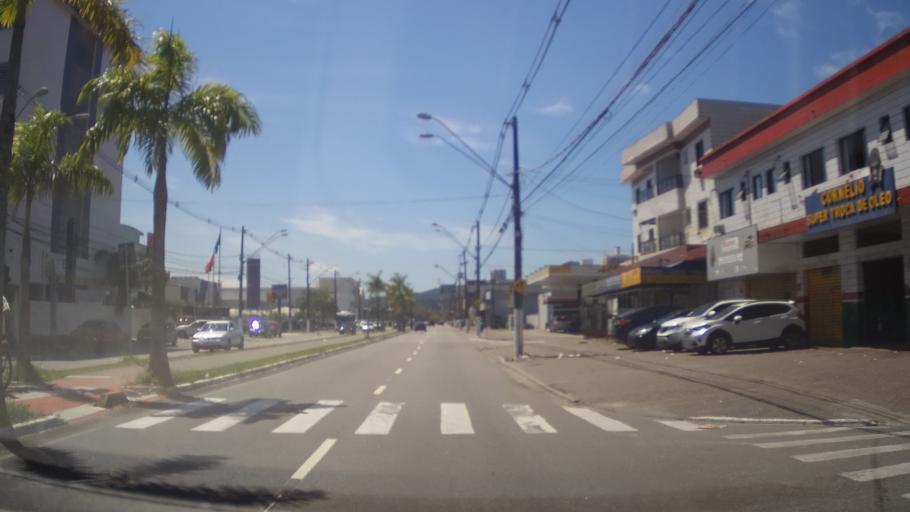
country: BR
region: Sao Paulo
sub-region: Praia Grande
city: Praia Grande
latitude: -24.0095
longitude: -46.4353
